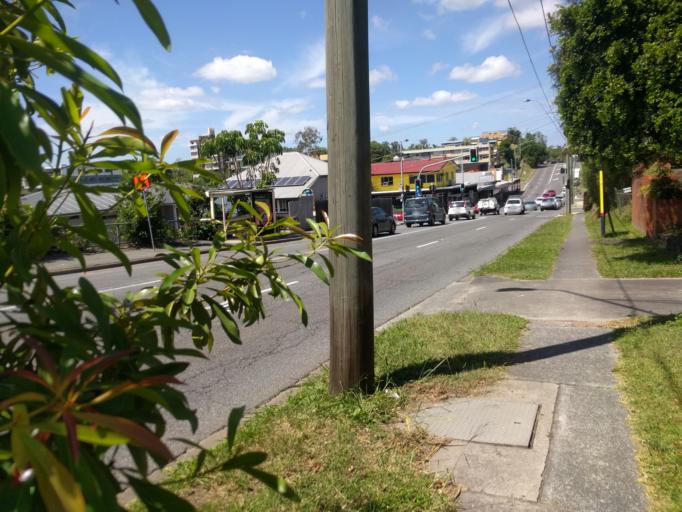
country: AU
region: Queensland
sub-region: Brisbane
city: Milton
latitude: -27.4733
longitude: 152.9962
